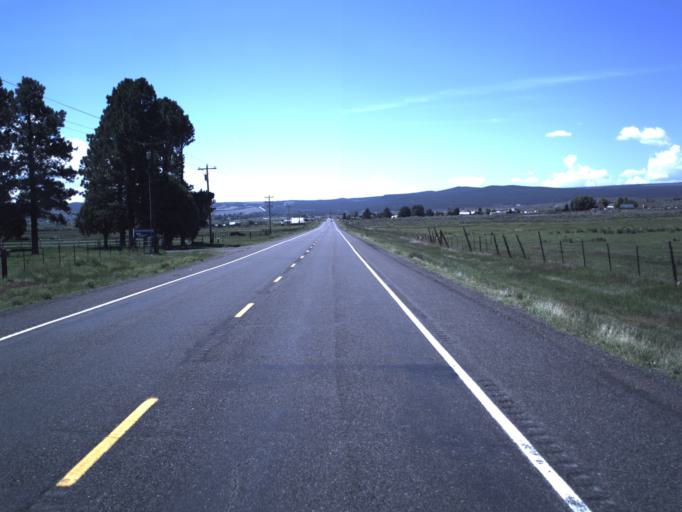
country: US
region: Utah
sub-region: Garfield County
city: Panguitch
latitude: 37.8688
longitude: -112.4376
